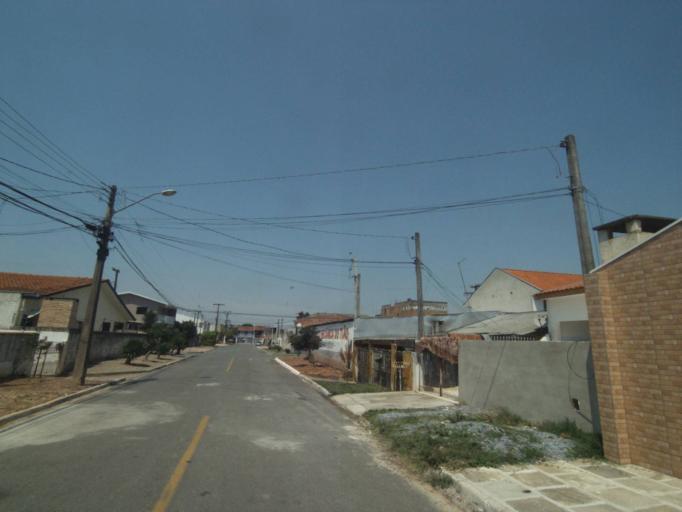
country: BR
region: Parana
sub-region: Sao Jose Dos Pinhais
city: Sao Jose dos Pinhais
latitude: -25.5202
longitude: -49.2673
